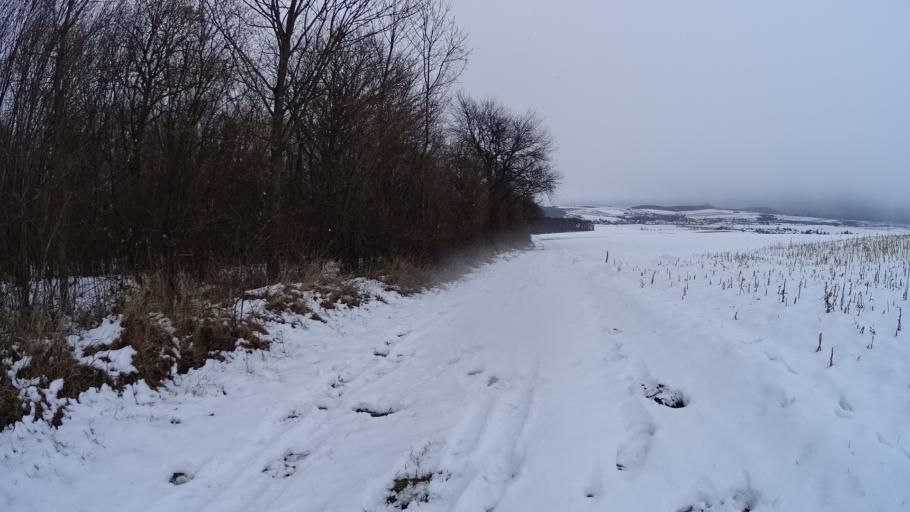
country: AT
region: Lower Austria
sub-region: Politischer Bezirk Korneuburg
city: Niederhollabrunn
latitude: 48.4168
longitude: 16.2762
